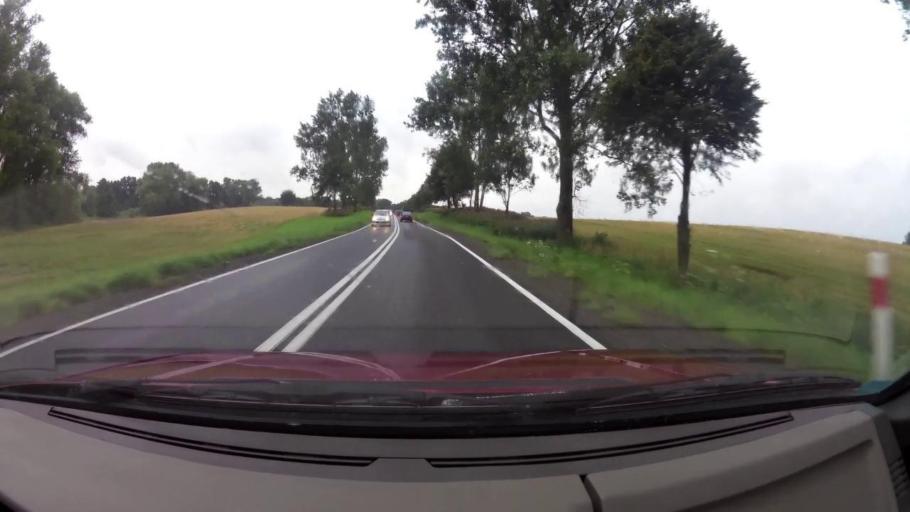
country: PL
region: West Pomeranian Voivodeship
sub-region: Powiat stargardzki
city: Marianowo
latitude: 53.4124
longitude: 15.2337
